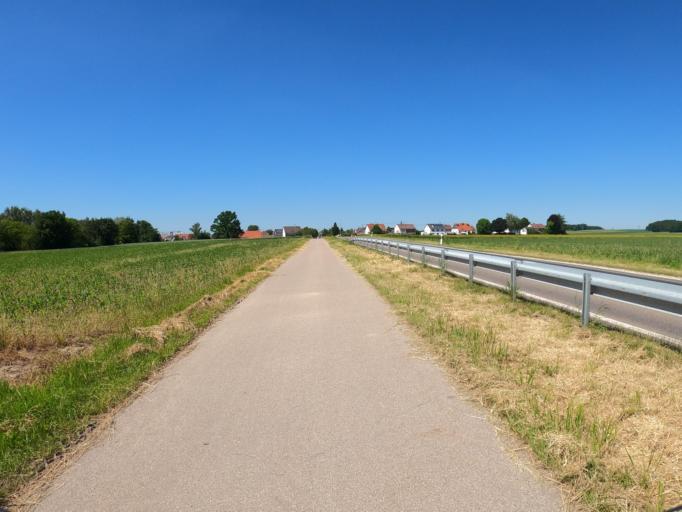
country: DE
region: Bavaria
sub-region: Swabia
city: Pfaffenhofen an der Roth
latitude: 48.3739
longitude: 10.1521
